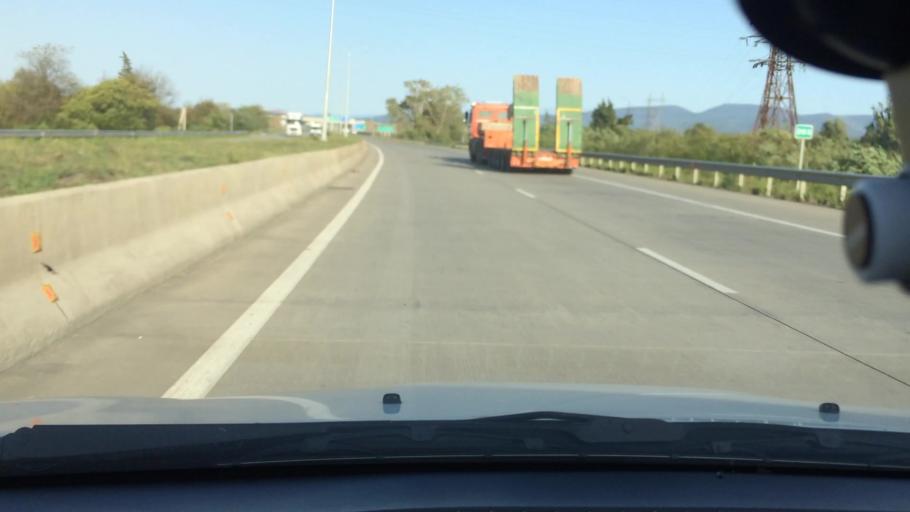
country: GE
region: Imereti
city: Zestap'oni
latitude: 42.1542
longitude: 42.9573
